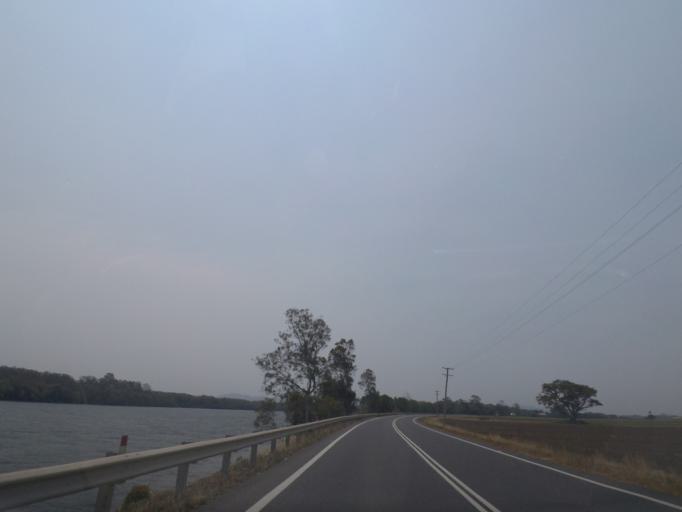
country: AU
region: New South Wales
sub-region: Richmond Valley
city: Evans Head
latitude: -28.9752
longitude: 153.4612
